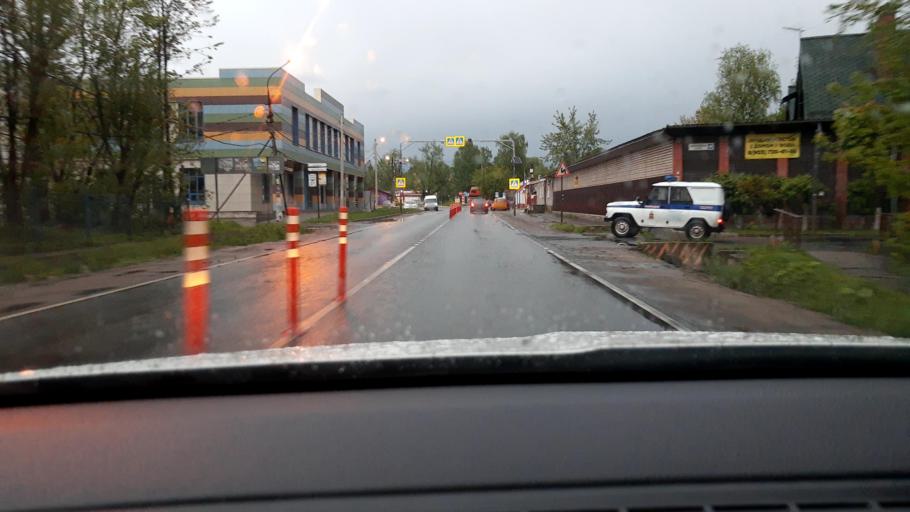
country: RU
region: Moskovskaya
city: Zagoryanskiy
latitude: 55.9246
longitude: 37.9142
